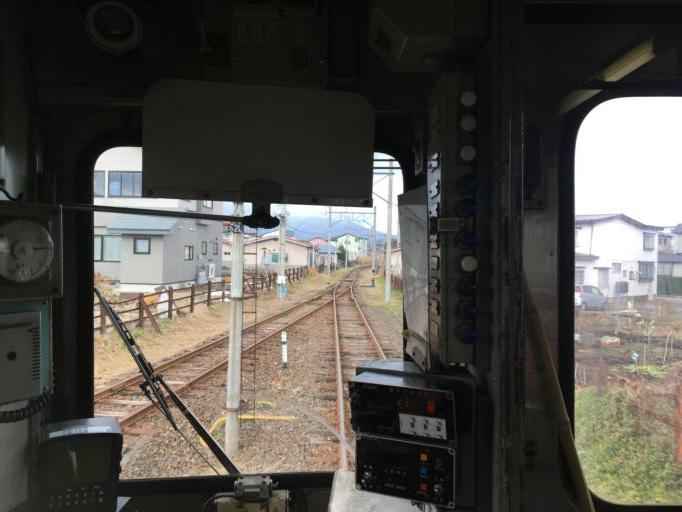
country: JP
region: Aomori
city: Hirosaki
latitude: 40.5676
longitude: 140.4799
